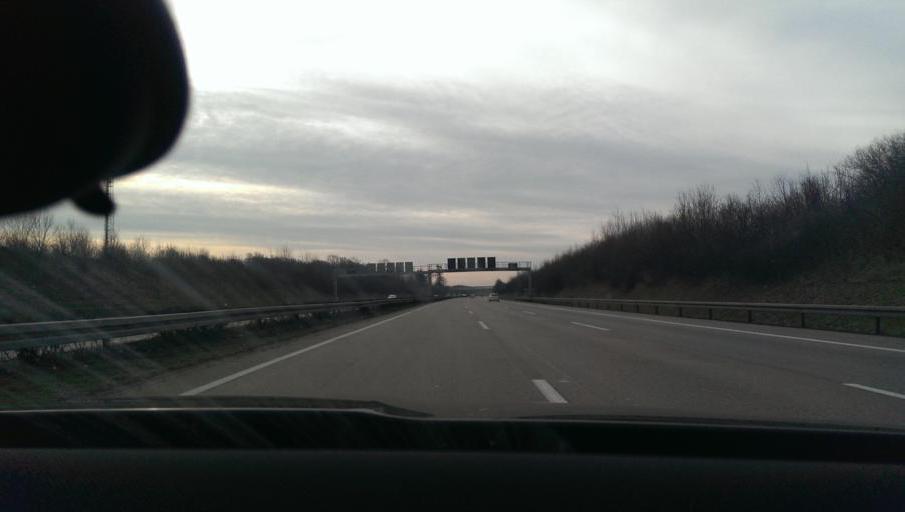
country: DE
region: Lower Saxony
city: Isernhagen Farster Bauerschaft
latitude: 52.4790
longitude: 9.8499
